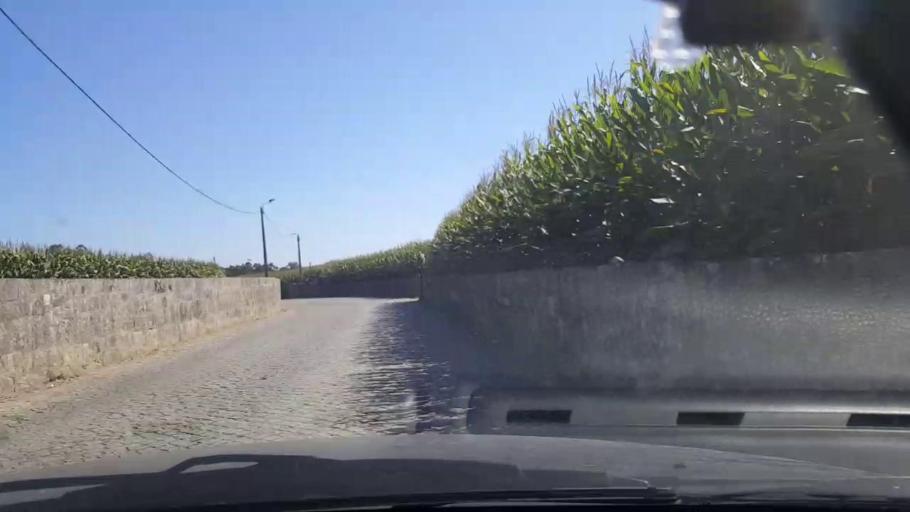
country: PT
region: Porto
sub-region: Vila do Conde
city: Arvore
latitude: 41.3173
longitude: -8.6920
